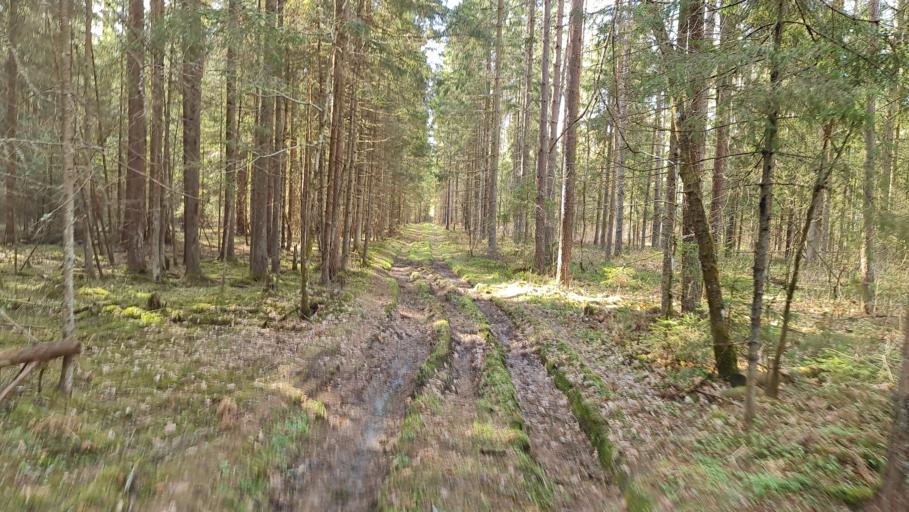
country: BY
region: Vitebsk
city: Byahoml'
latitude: 54.6903
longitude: 27.9927
